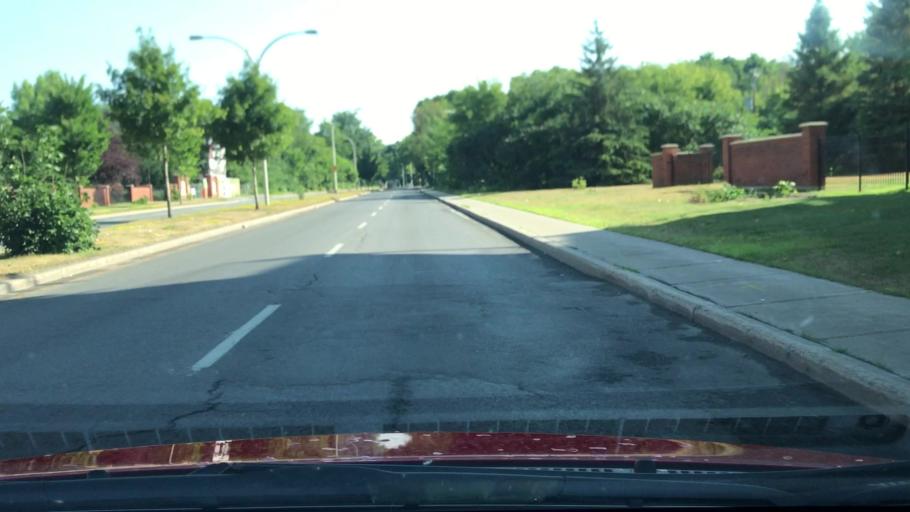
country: CA
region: Quebec
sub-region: Laval
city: Laval
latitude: 45.5463
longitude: -73.7348
